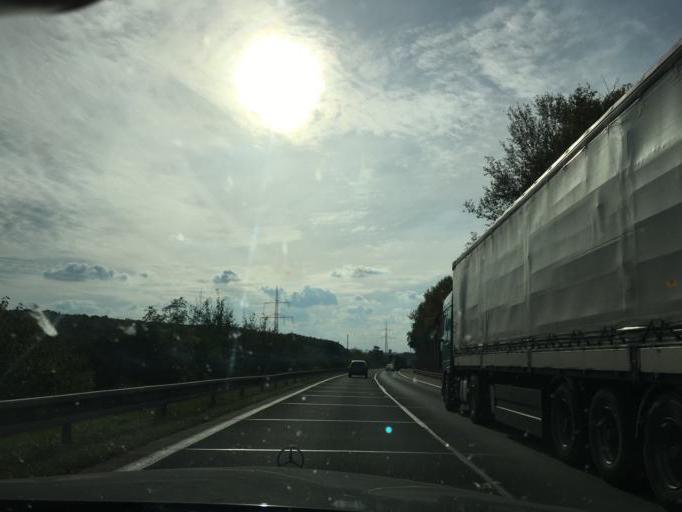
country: CZ
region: Praha
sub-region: Praha 20
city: Horni Pocernice
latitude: 50.1002
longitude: 14.6096
